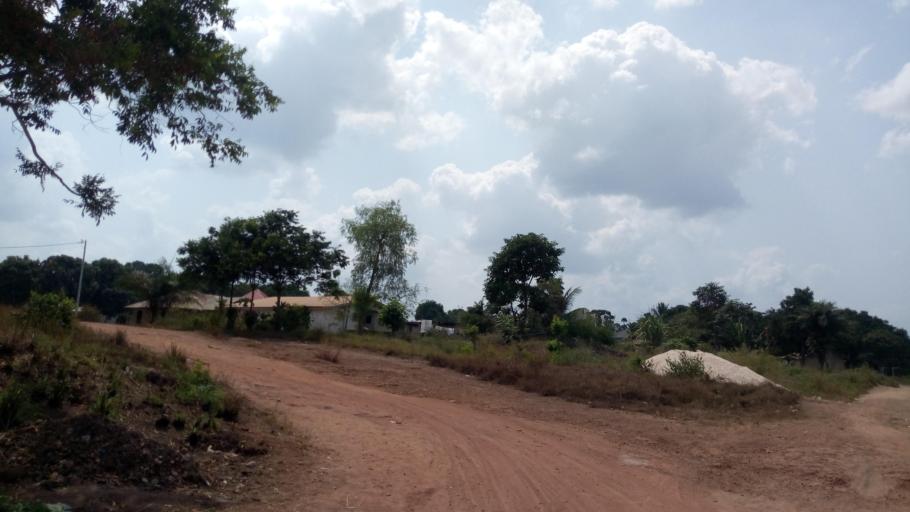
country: SL
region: Southern Province
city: Mogbwemo
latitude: 7.7934
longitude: -12.3016
